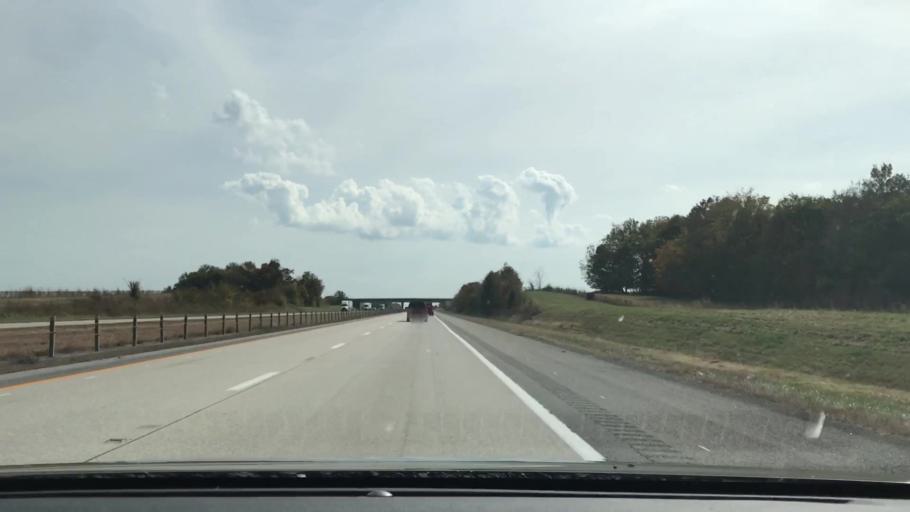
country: US
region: Kentucky
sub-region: Christian County
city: Hopkinsville
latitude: 36.8098
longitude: -87.6213
